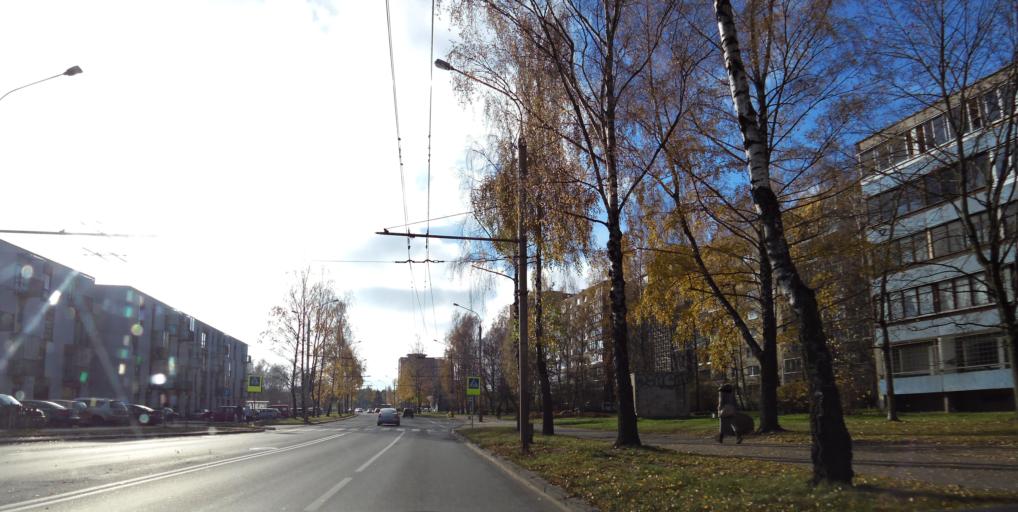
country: LT
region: Vilnius County
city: Lazdynai
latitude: 54.6873
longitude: 25.2070
